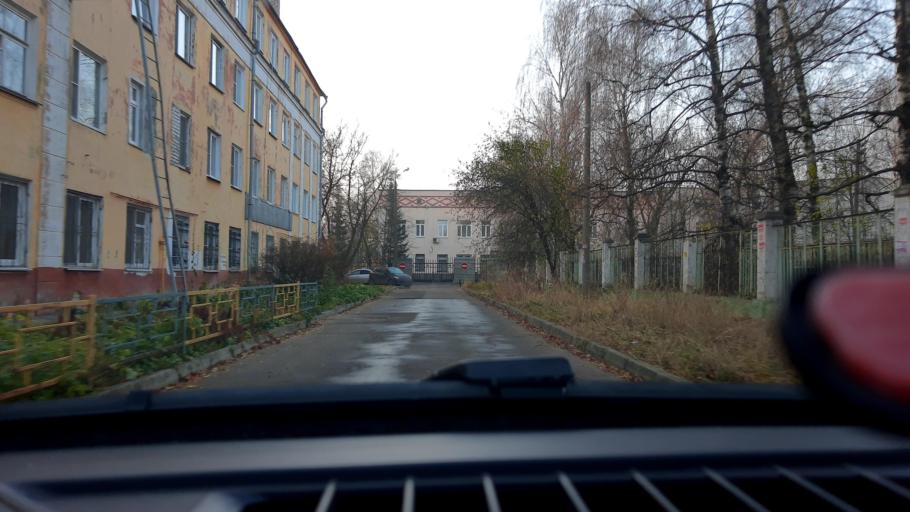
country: RU
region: Nizjnij Novgorod
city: Gorbatovka
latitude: 56.3291
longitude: 43.8481
